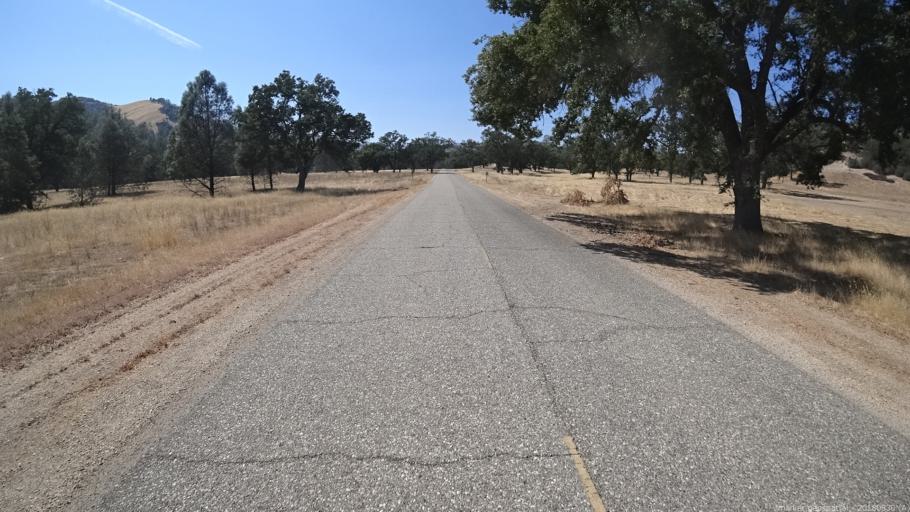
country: US
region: California
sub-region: Monterey County
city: King City
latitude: 36.0052
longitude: -121.2718
